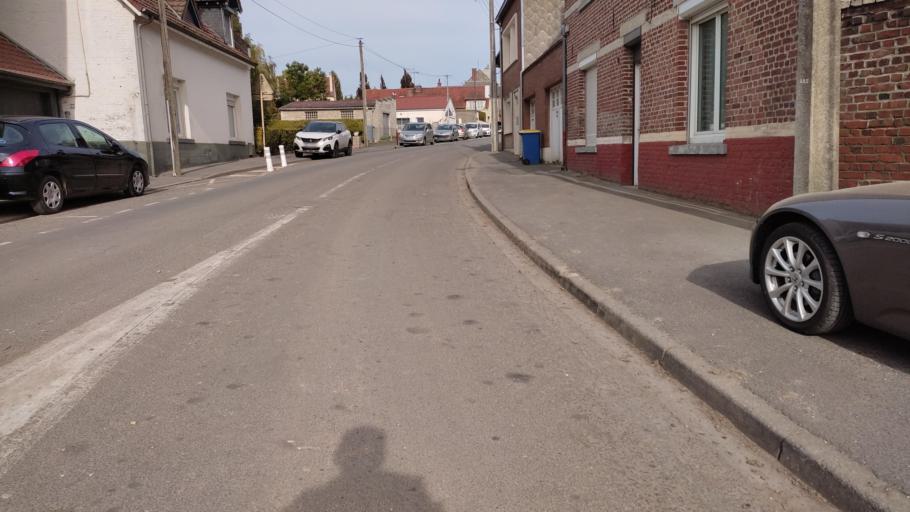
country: FR
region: Nord-Pas-de-Calais
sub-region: Departement du Pas-de-Calais
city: Feuchy
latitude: 50.3024
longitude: 2.8359
